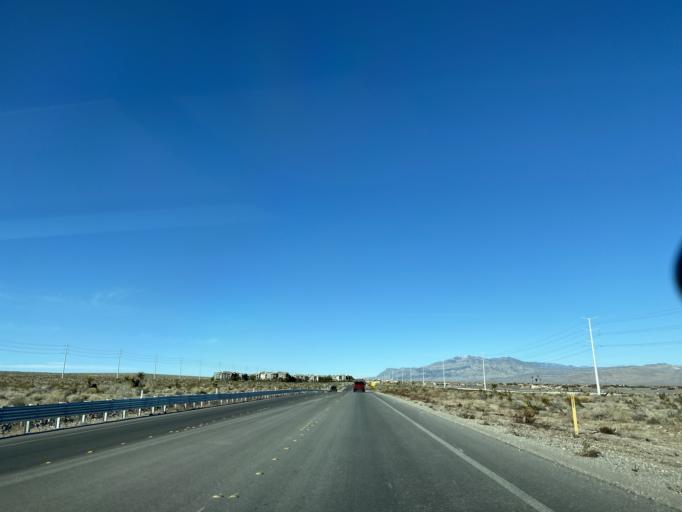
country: US
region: Nevada
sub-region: Clark County
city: Summerlin South
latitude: 36.2673
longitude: -115.3300
